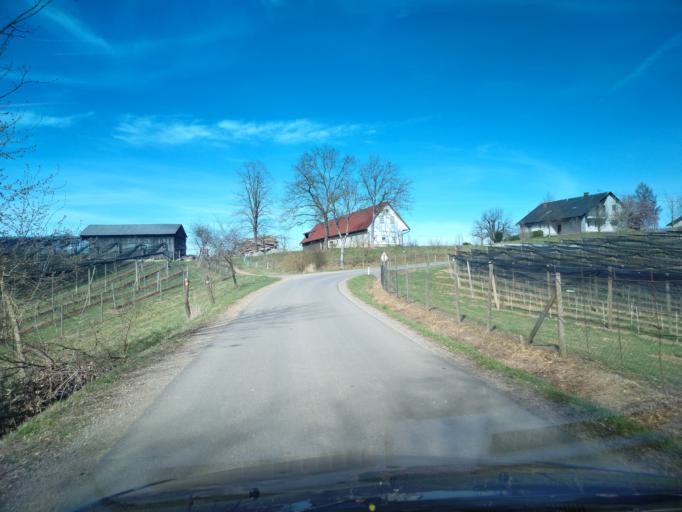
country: AT
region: Styria
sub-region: Politischer Bezirk Deutschlandsberg
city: Unterbergla
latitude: 46.7982
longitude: 15.3149
